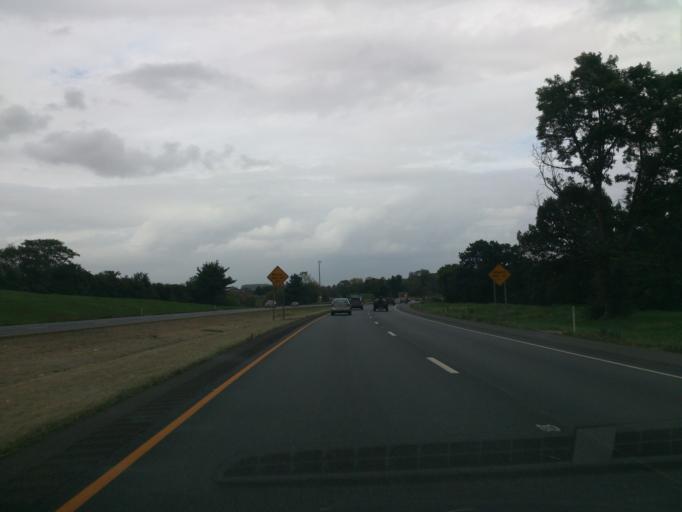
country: US
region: Pennsylvania
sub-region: Lancaster County
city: Brownstown
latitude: 40.1017
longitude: -76.2564
